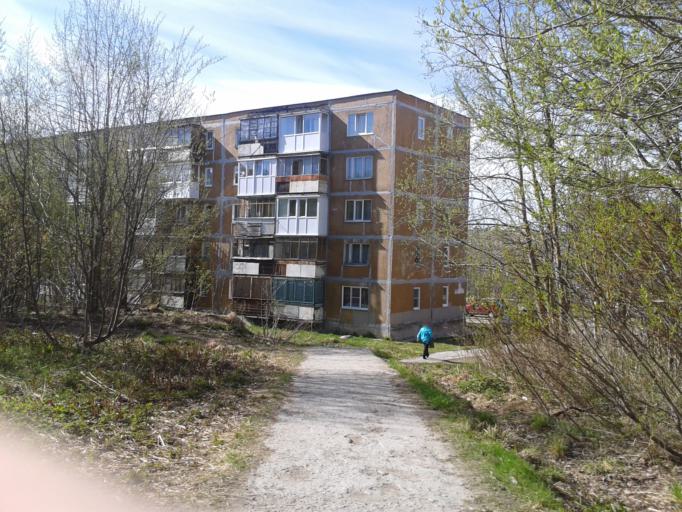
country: RU
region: Murmansk
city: Polyarnyye Zori
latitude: 67.3677
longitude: 32.4960
